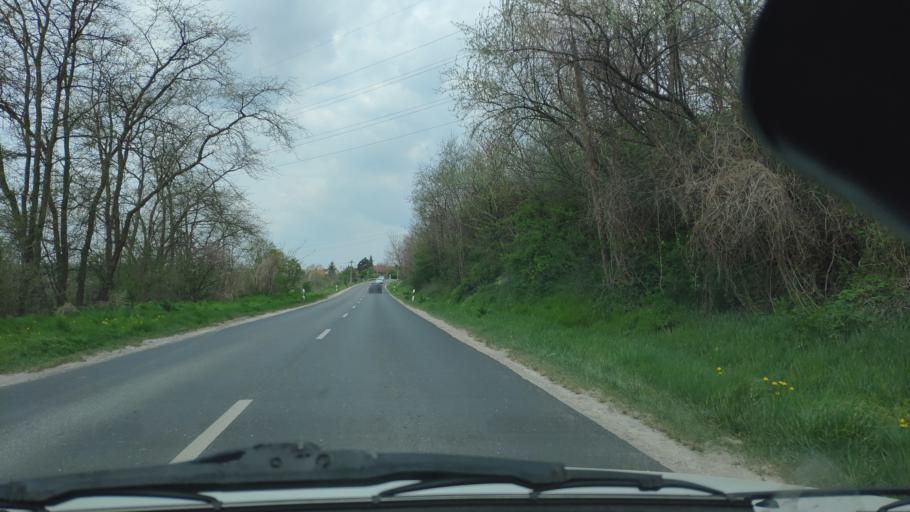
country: HU
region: Pest
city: Biatorbagy
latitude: 47.4552
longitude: 18.8155
